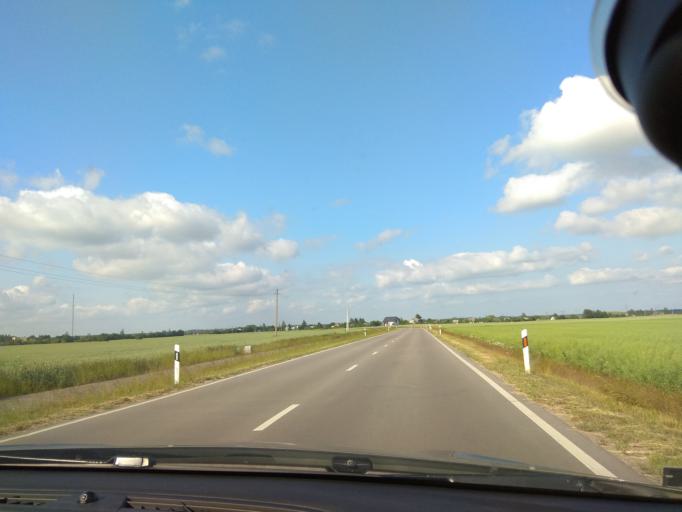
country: LT
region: Siauliu apskritis
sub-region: Joniskis
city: Joniskis
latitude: 56.2318
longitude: 23.6328
